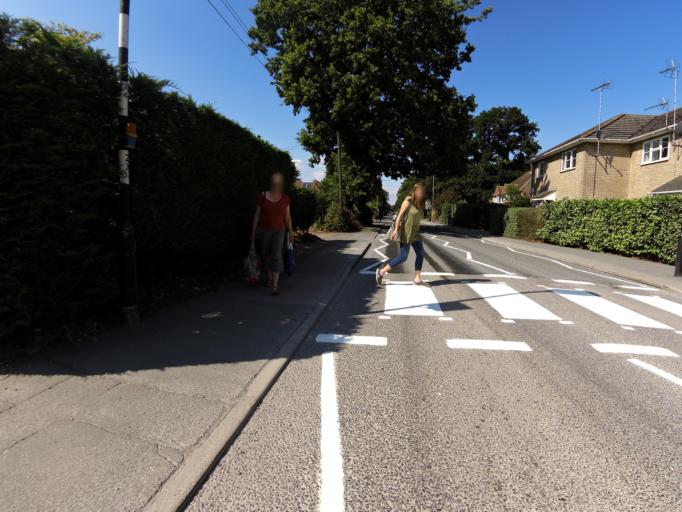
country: GB
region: England
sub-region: Essex
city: West Bergholt
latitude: 51.8836
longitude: 0.8541
